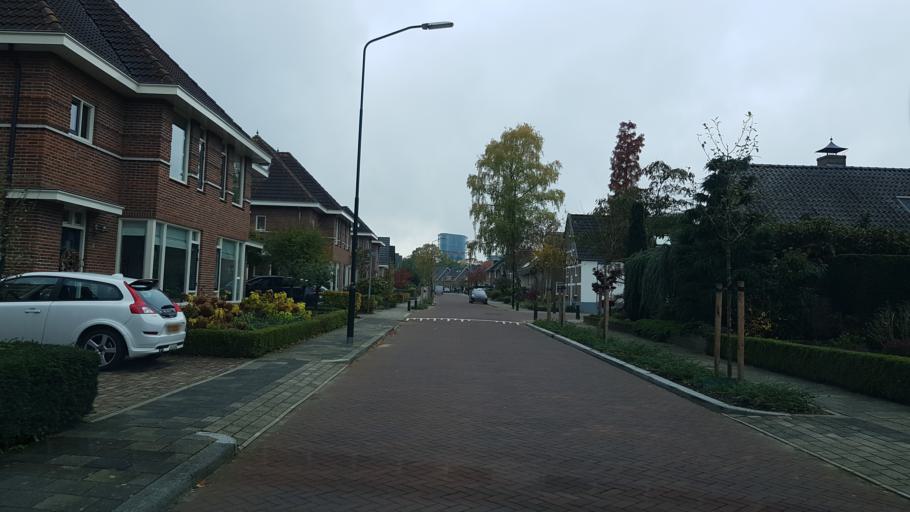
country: NL
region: Gelderland
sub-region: Gemeente Apeldoorn
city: Apeldoorn
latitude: 52.2169
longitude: 5.9438
